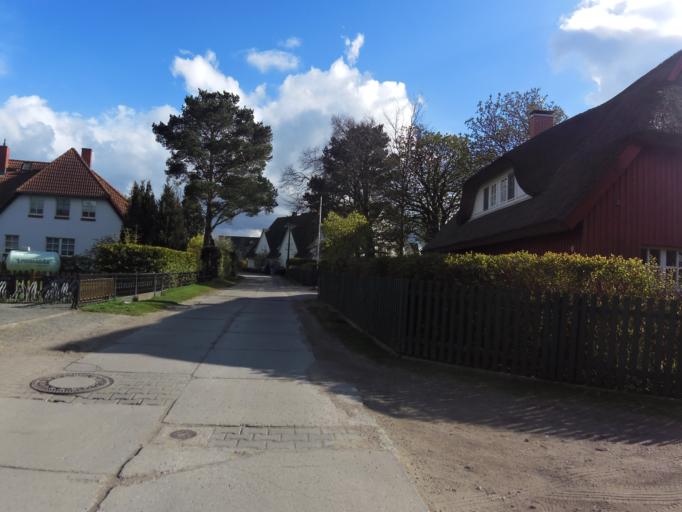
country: DE
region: Mecklenburg-Vorpommern
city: Zingst
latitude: 54.4381
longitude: 12.6956
